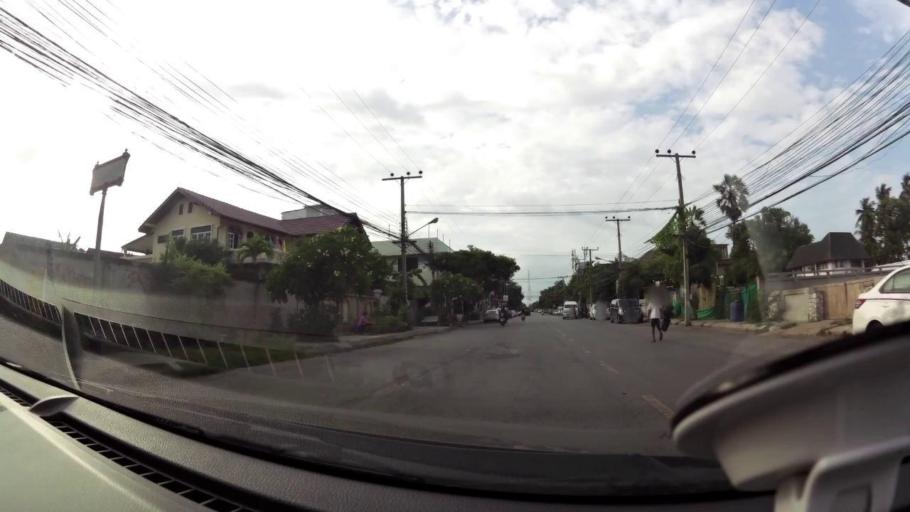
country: TH
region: Prachuap Khiri Khan
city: Hua Hin
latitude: 12.5784
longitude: 99.9562
